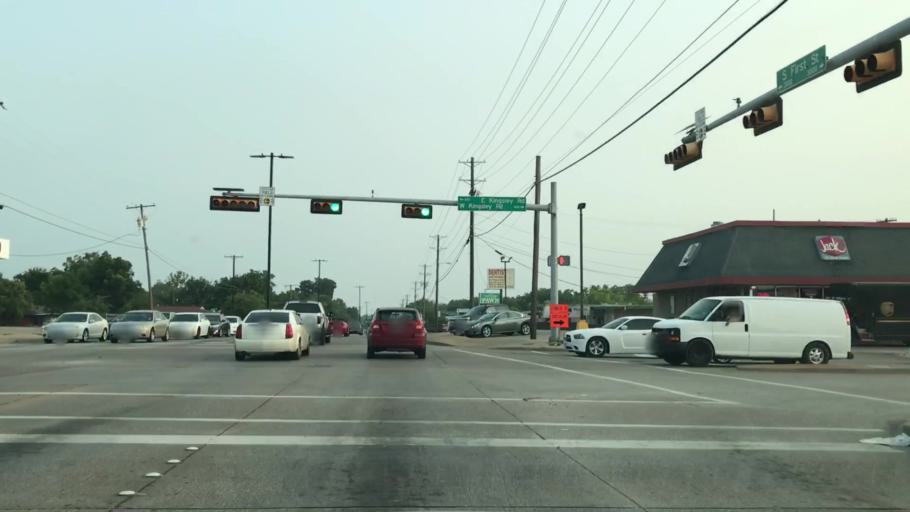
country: US
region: Texas
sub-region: Dallas County
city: Garland
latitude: 32.8789
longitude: -96.6310
